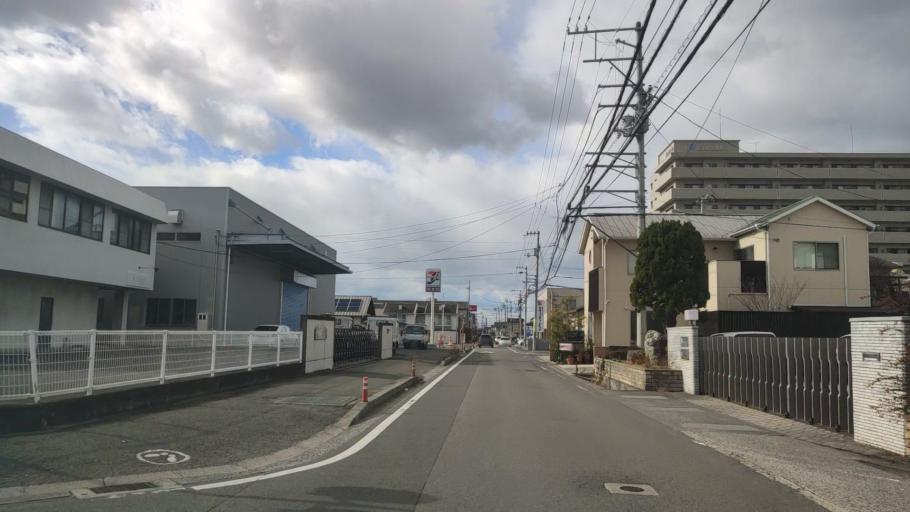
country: JP
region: Ehime
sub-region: Shikoku-chuo Shi
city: Matsuyama
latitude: 33.8098
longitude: 132.7940
